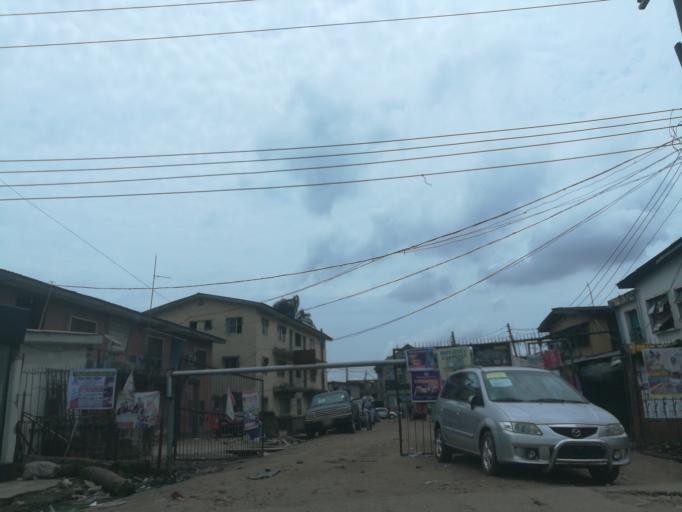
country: NG
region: Lagos
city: Somolu
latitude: 6.5325
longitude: 3.3887
